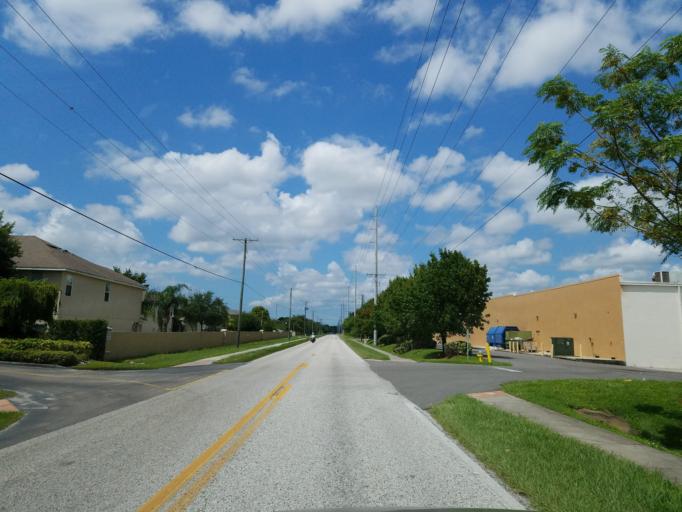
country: US
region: Florida
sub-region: Hillsborough County
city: Palm River-Clair Mel
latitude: 27.9412
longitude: -82.3381
